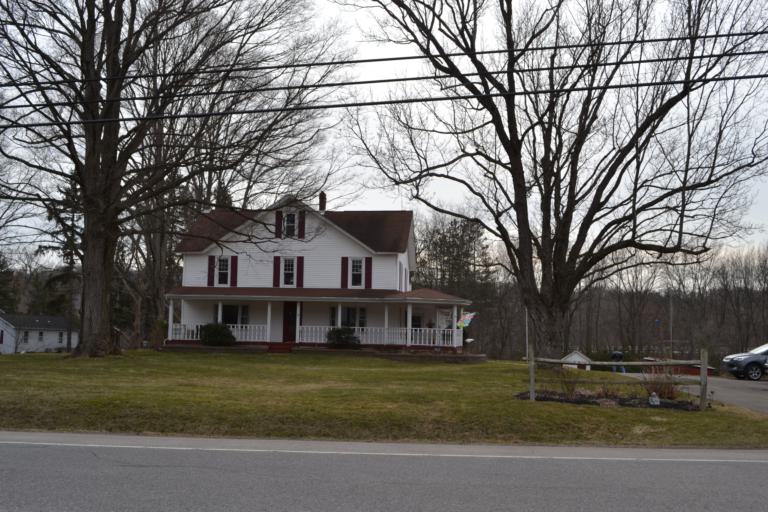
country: US
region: New York
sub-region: Erie County
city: East Aurora
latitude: 42.7313
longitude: -78.5914
